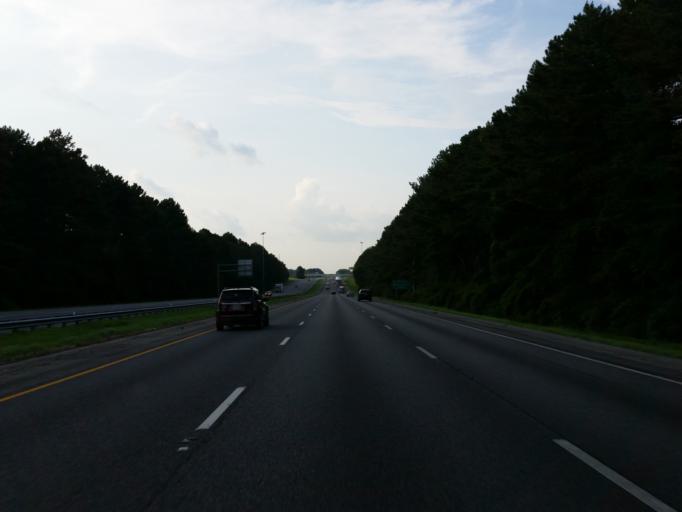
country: US
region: Georgia
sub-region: Houston County
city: Perry
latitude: 32.4829
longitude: -83.7422
